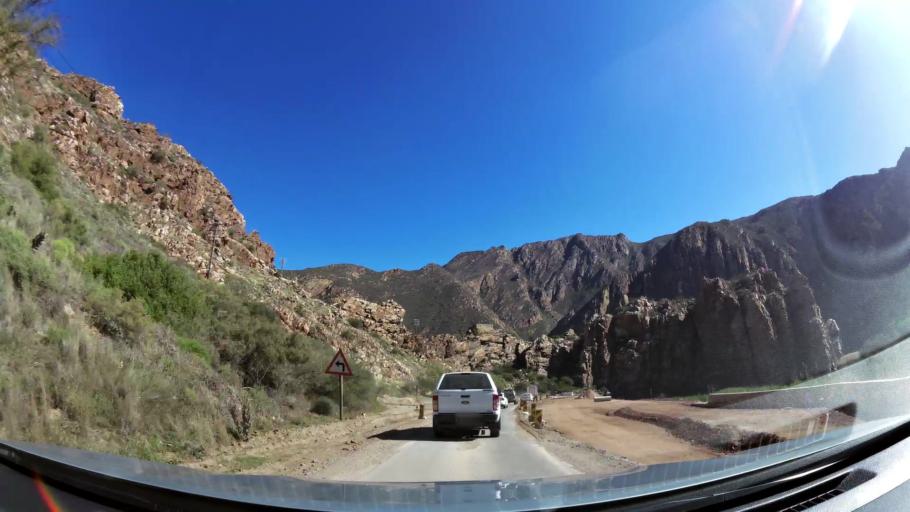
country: ZA
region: Western Cape
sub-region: Cape Winelands District Municipality
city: Ashton
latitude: -33.8031
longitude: 20.0963
